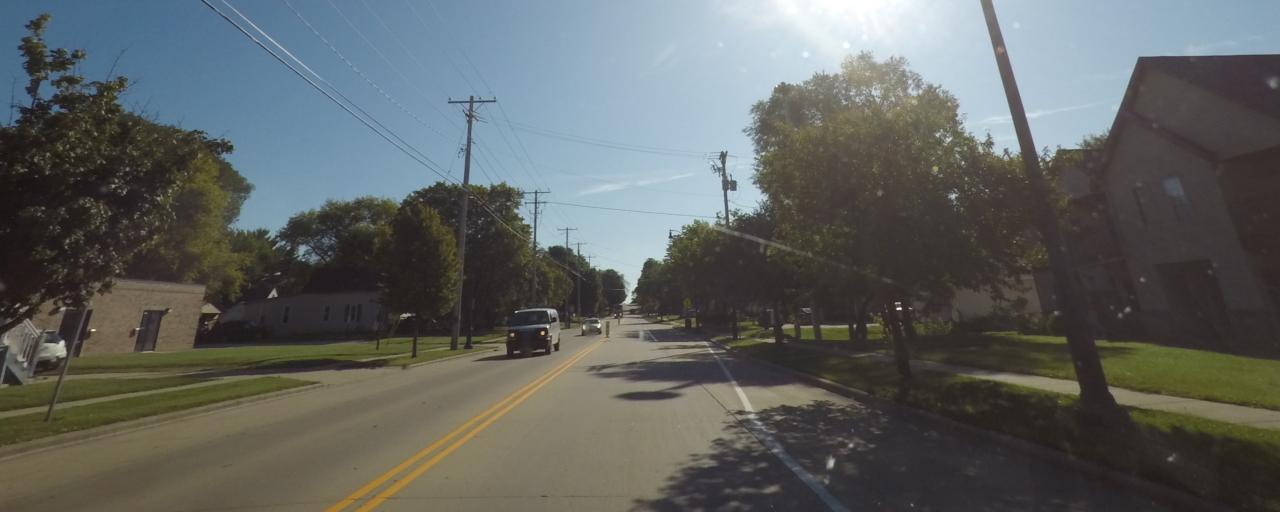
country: US
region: Wisconsin
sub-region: Jefferson County
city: Jefferson
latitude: 43.0057
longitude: -88.8185
